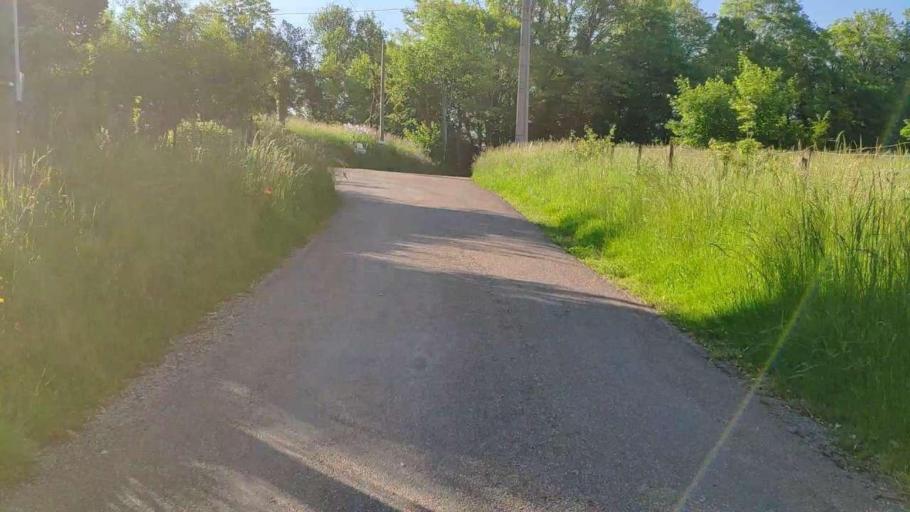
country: FR
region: Franche-Comte
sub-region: Departement du Jura
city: Perrigny
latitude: 46.7156
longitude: 5.6207
